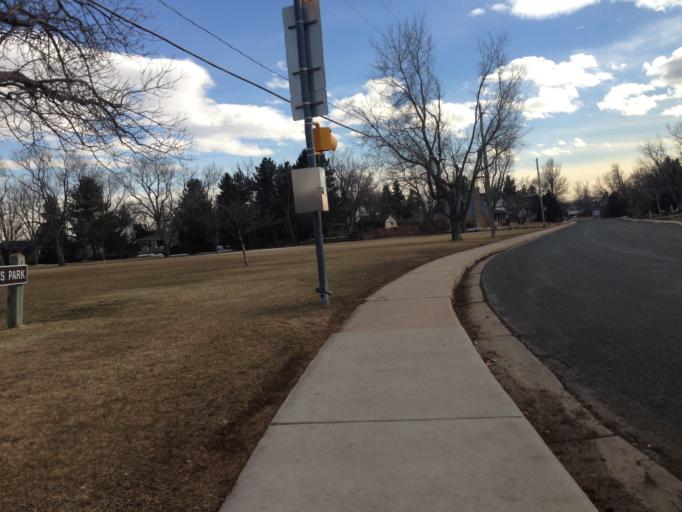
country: US
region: Colorado
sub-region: Boulder County
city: Boulder
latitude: 39.9931
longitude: -105.2290
